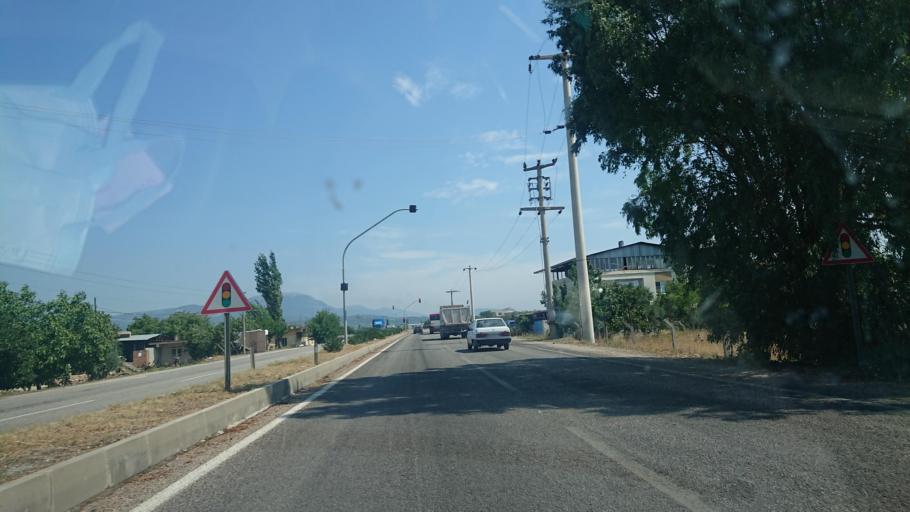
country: TR
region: Izmir
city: Torbali
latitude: 38.2134
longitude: 27.3686
